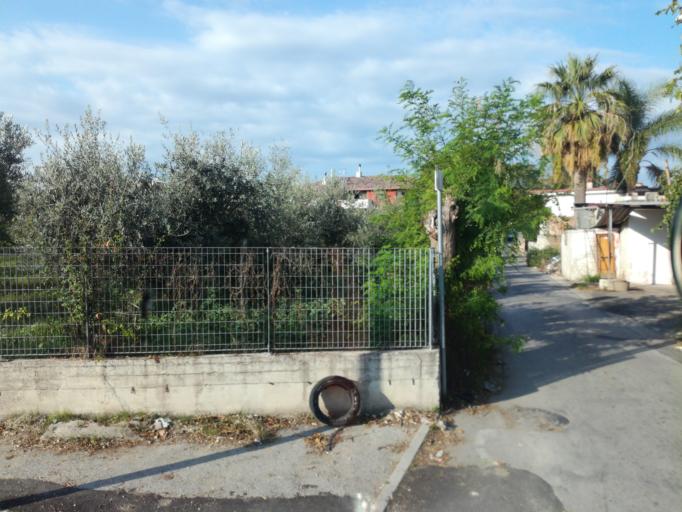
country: IT
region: Campania
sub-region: Provincia di Napoli
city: Giugliano in Campania
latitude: 40.9449
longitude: 14.1790
